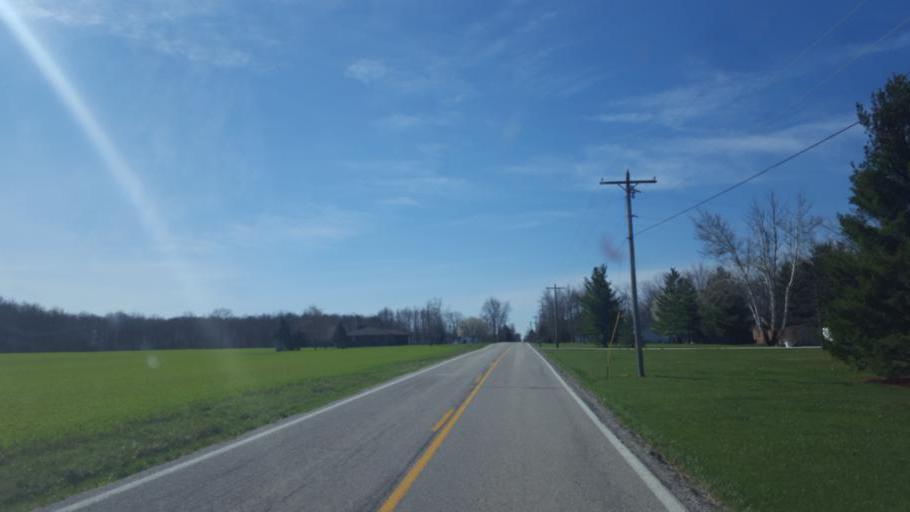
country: US
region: Ohio
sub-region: Morrow County
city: Cardington
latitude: 40.5529
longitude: -82.9624
